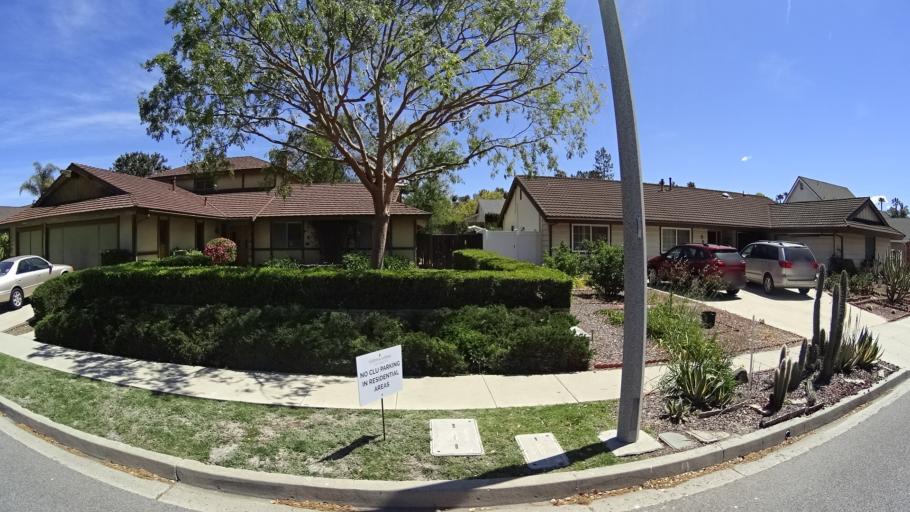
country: US
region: California
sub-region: Ventura County
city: Moorpark
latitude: 34.2288
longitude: -118.8757
